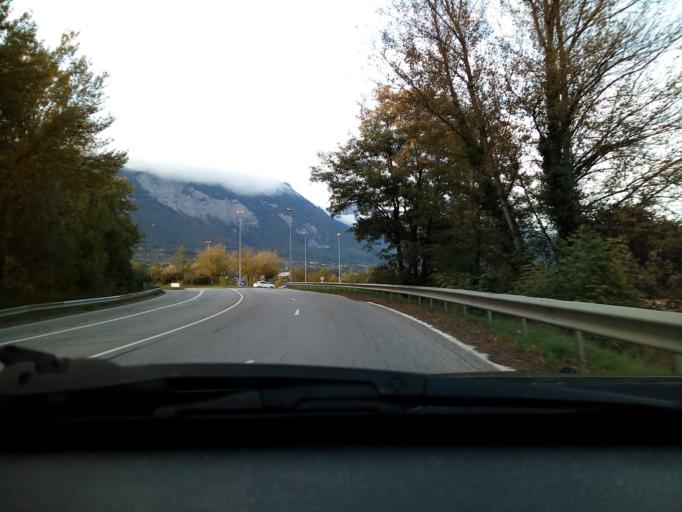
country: FR
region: Rhone-Alpes
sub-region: Departement de l'Isere
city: Montbonnot-Saint-Martin
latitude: 45.2211
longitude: 5.8228
